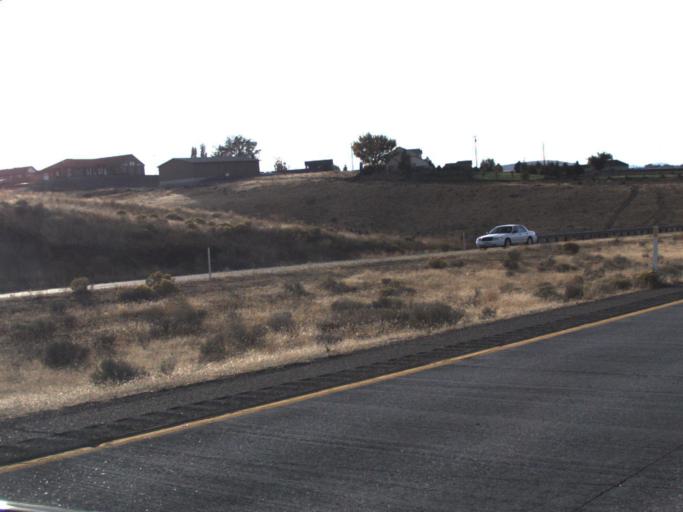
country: US
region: Washington
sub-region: Franklin County
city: West Pasco
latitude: 46.1869
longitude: -119.2530
